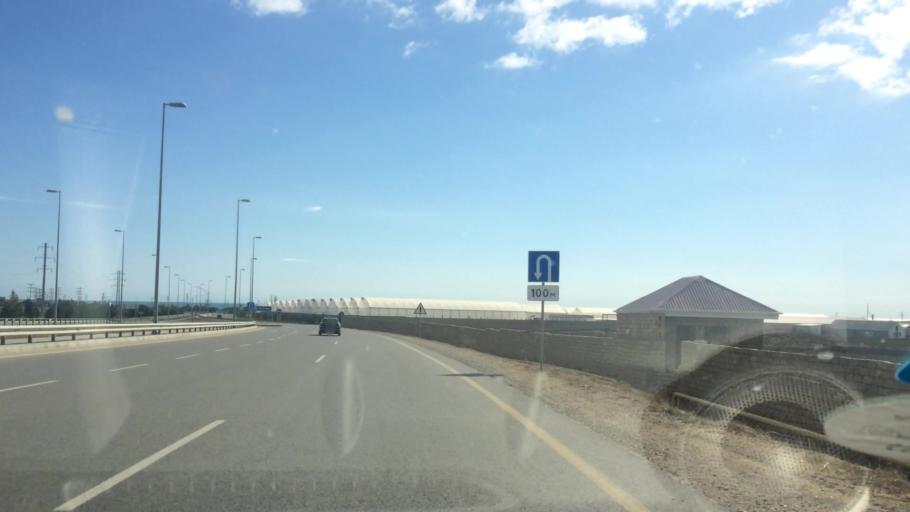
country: AZ
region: Baki
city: Zyrya
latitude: 40.3988
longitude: 50.3227
